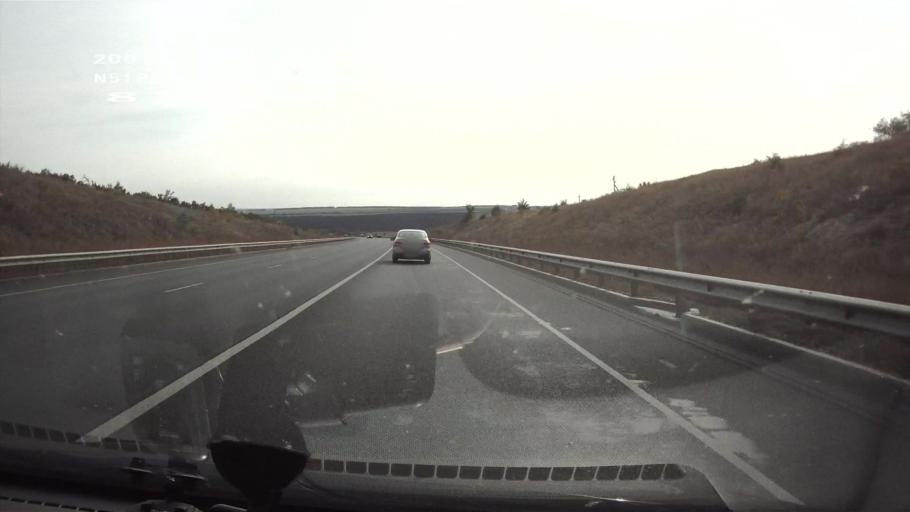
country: RU
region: Saratov
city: Yelshanka
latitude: 51.8849
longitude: 46.5149
